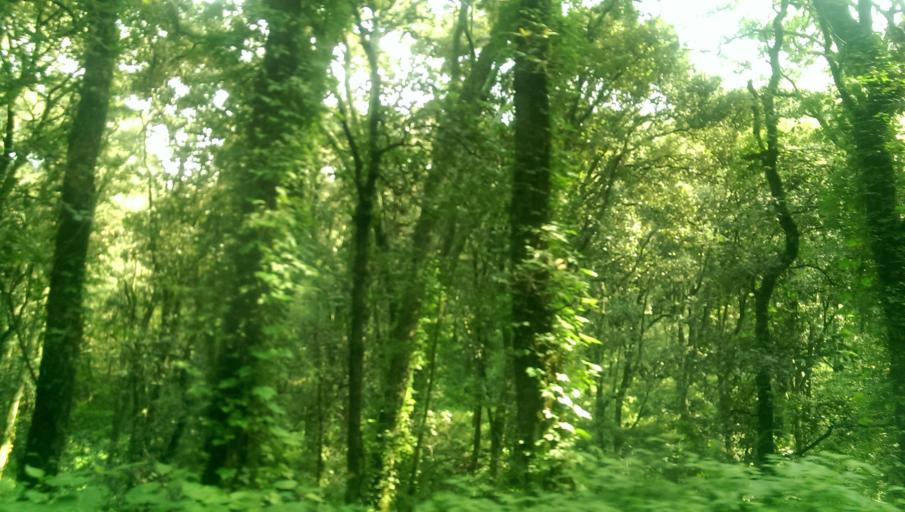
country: MX
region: Mexico
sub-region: Jilotepec
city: Jilotepec de Molina Enriquez
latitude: 19.9219
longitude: -99.4920
